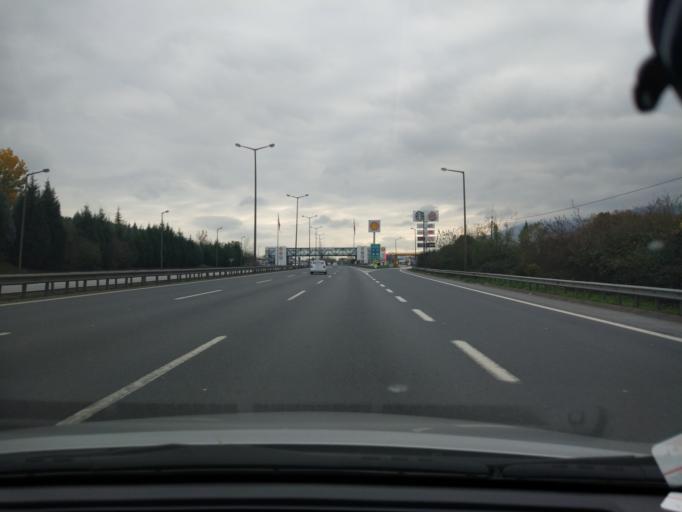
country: TR
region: Kocaeli
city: Derbent
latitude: 40.7286
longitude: 30.0660
